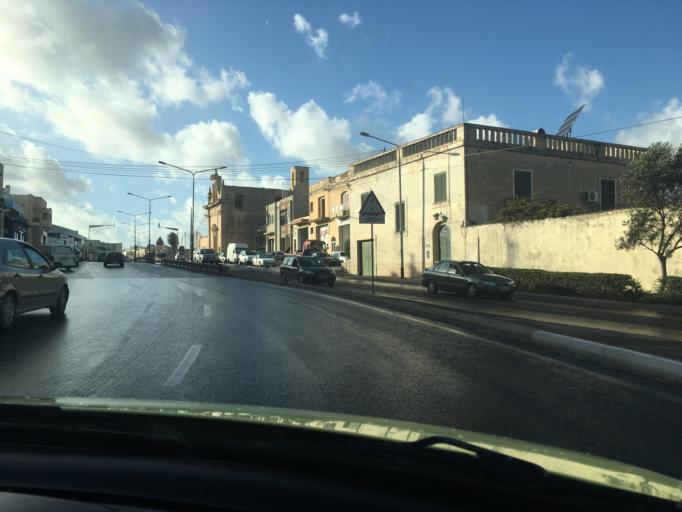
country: MT
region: Haz-Zebbug
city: Haz-Zebbug
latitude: 35.8733
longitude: 14.4520
